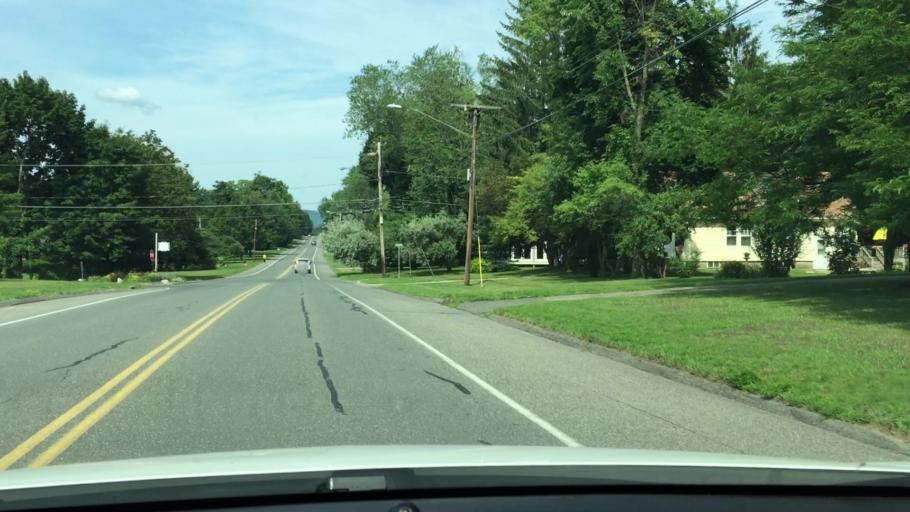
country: US
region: Massachusetts
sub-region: Berkshire County
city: Pittsfield
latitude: 42.4341
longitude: -73.2248
